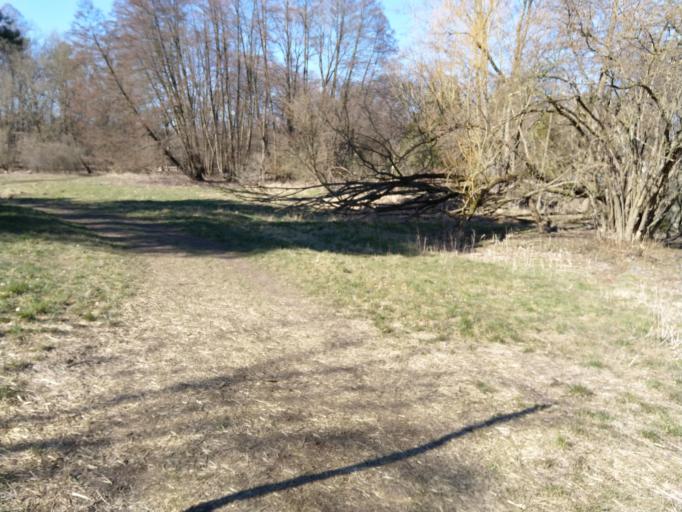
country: DE
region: Brandenburg
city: Grunheide
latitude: 52.4149
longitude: 13.8010
